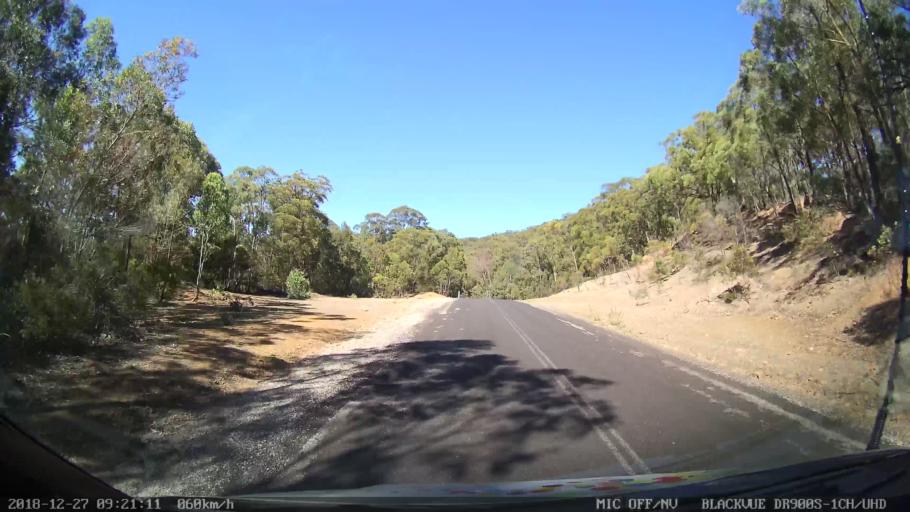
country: AU
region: New South Wales
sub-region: Lithgow
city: Portland
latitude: -33.1222
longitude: 150.0184
